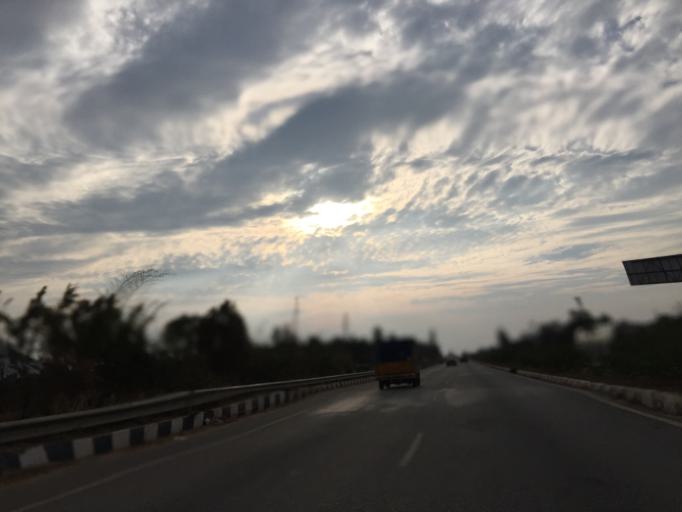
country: IN
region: Karnataka
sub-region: Kolar
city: Mulbagal
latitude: 13.1538
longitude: 78.3285
